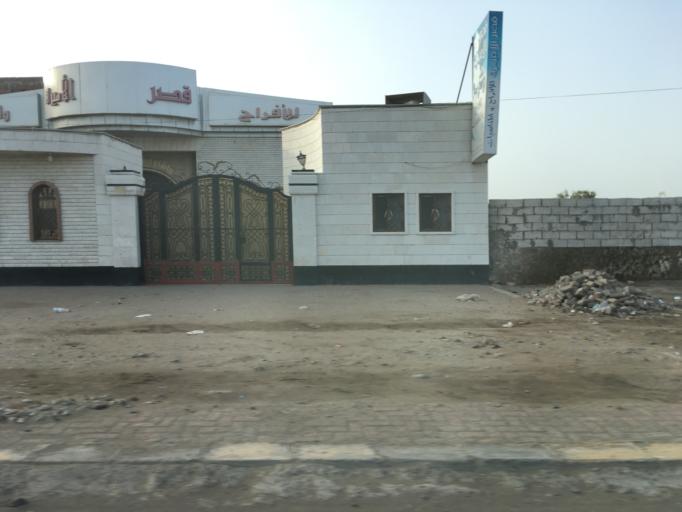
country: YE
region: Aden
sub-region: Ash Shaikh Outhman
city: Ash Shaykh `Uthman
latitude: 12.8594
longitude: 45.0082
